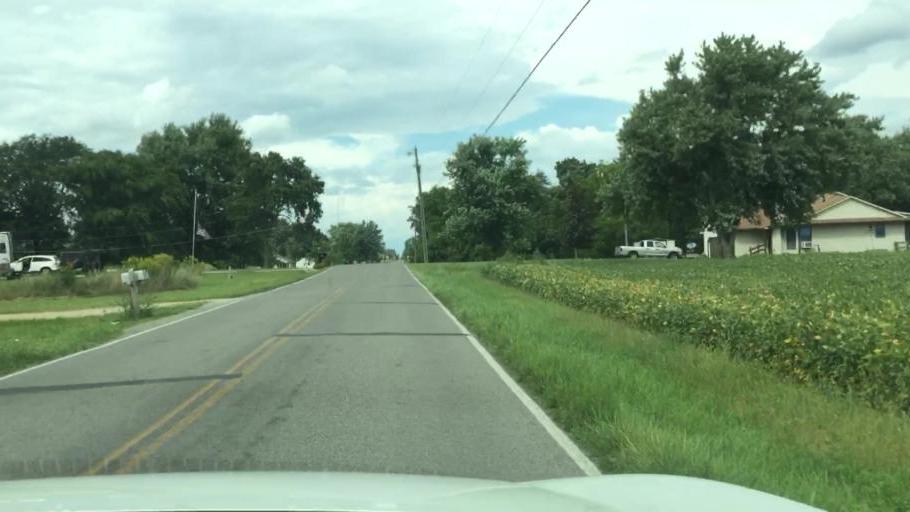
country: US
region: Ohio
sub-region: Champaign County
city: Urbana
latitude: 40.0936
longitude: -83.7138
